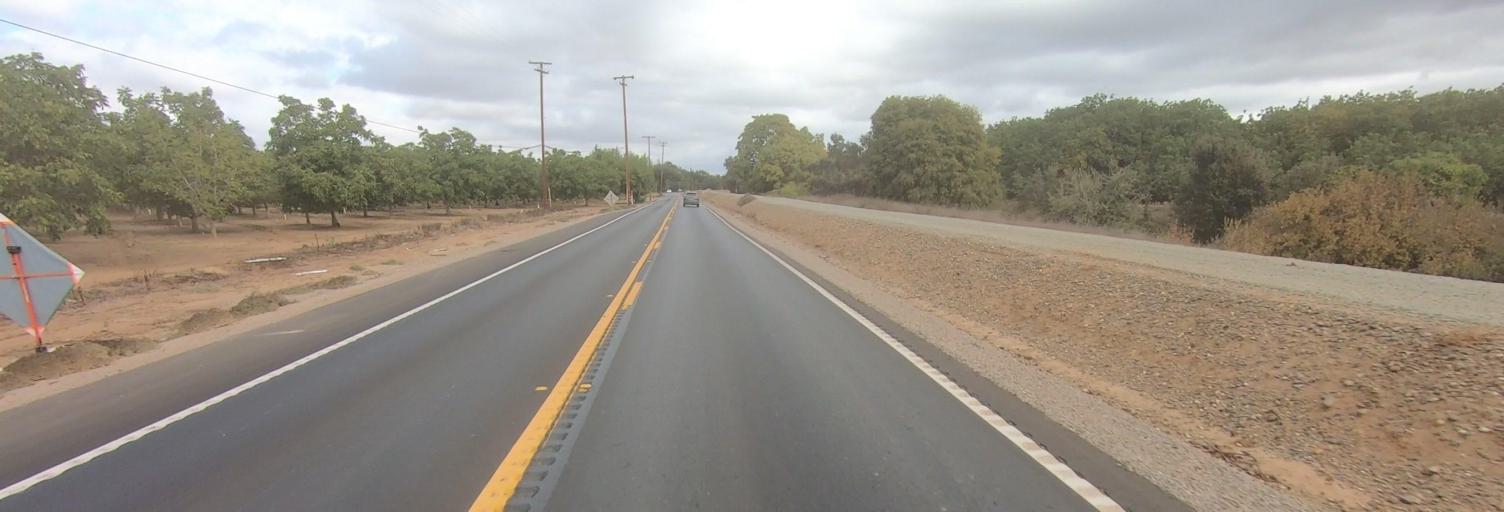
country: US
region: California
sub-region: San Joaquin County
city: Linden
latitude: 38.0426
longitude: -121.0267
